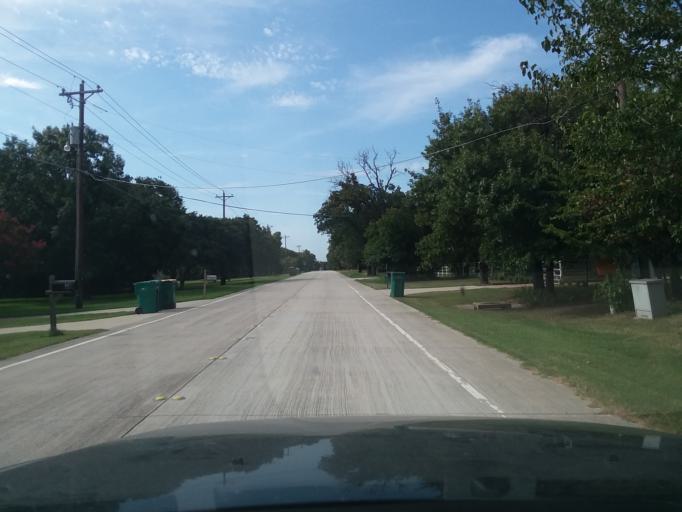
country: US
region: Texas
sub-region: Denton County
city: Double Oak
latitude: 33.0681
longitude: -97.1142
